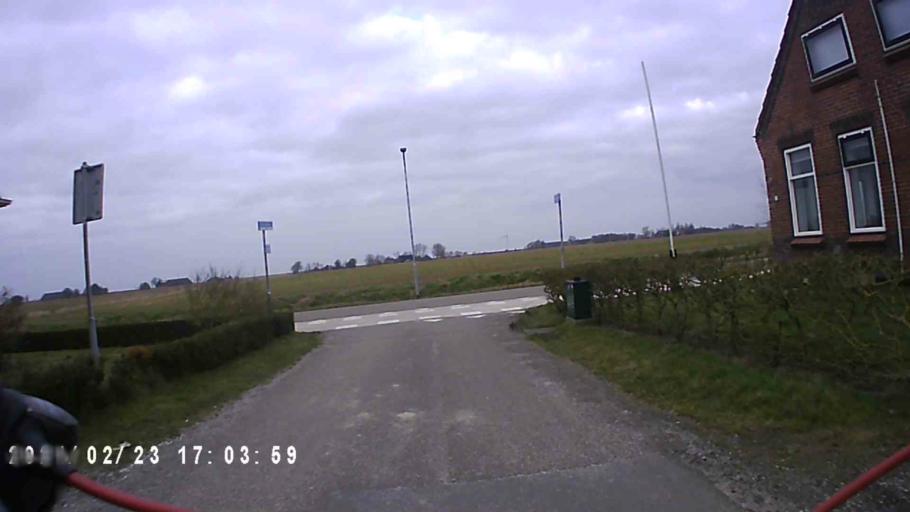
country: NL
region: Groningen
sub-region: Gemeente De Marne
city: Ulrum
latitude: 53.3878
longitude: 6.3843
